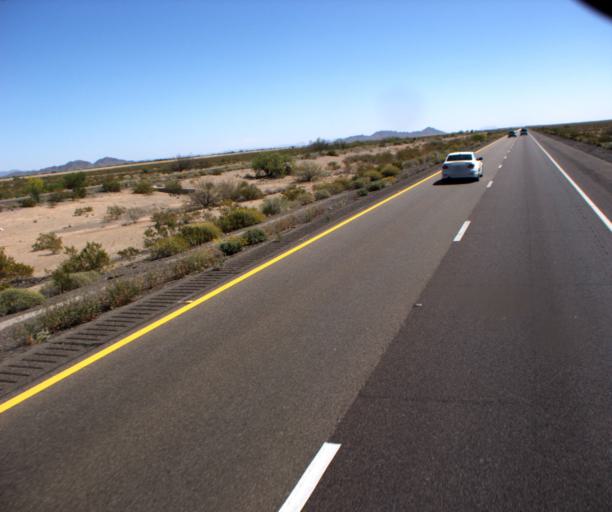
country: US
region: Arizona
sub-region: La Paz County
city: Salome
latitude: 33.6029
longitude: -113.5801
